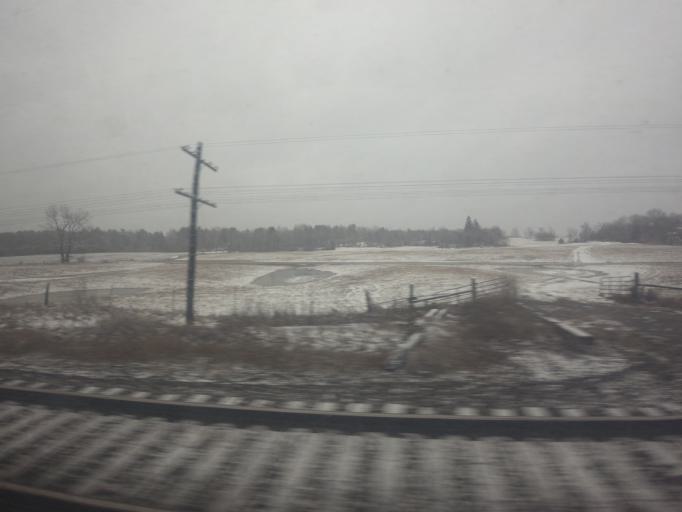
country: US
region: New York
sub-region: Jefferson County
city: Alexandria Bay
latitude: 44.5015
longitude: -75.8597
